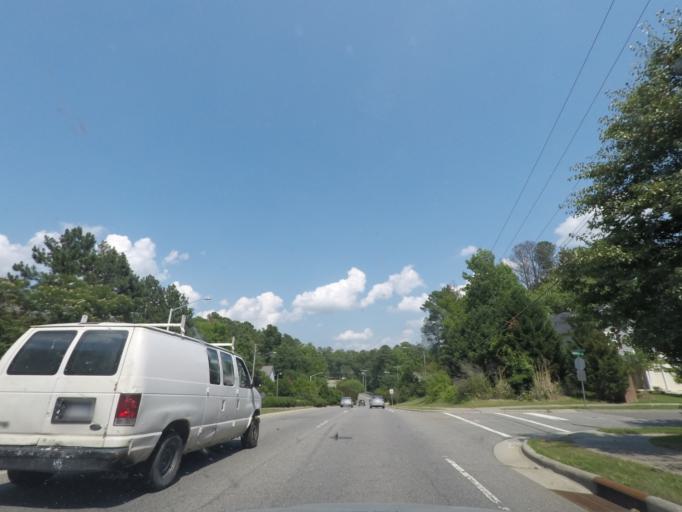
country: US
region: North Carolina
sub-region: Durham County
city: Durham
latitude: 35.9582
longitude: -78.9466
